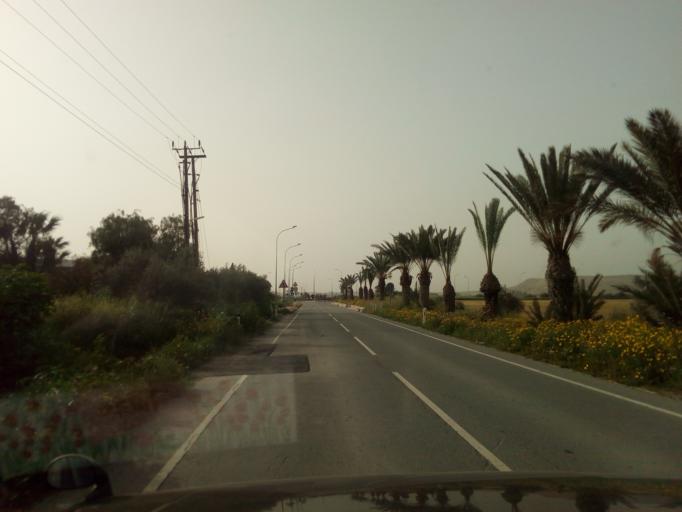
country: CY
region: Larnaka
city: Athienou
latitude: 35.0578
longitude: 33.5249
